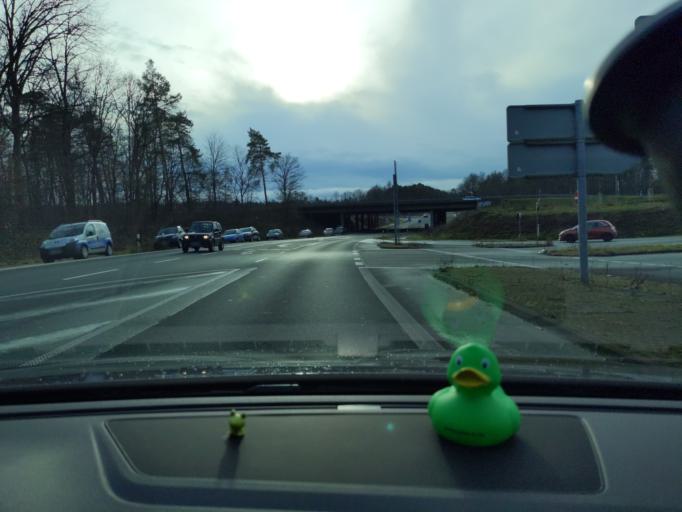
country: DE
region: North Rhine-Westphalia
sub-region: Regierungsbezirk Koln
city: Rath
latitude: 50.9159
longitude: 7.1072
